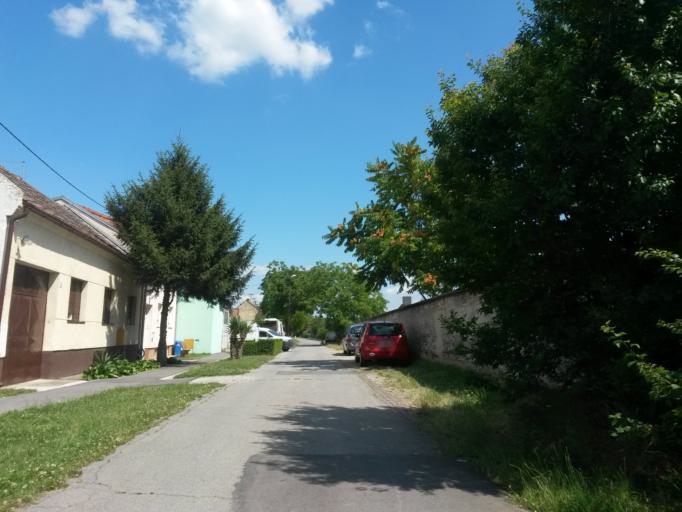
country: HR
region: Osjecko-Baranjska
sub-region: Grad Osijek
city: Osijek
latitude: 45.5518
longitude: 18.7252
